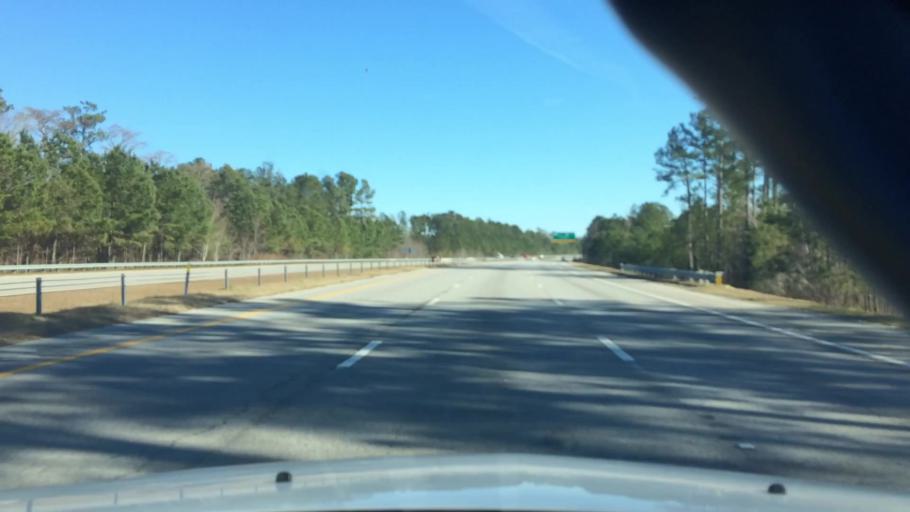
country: US
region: South Carolina
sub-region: Horry County
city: North Myrtle Beach
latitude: 33.8662
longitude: -78.6929
